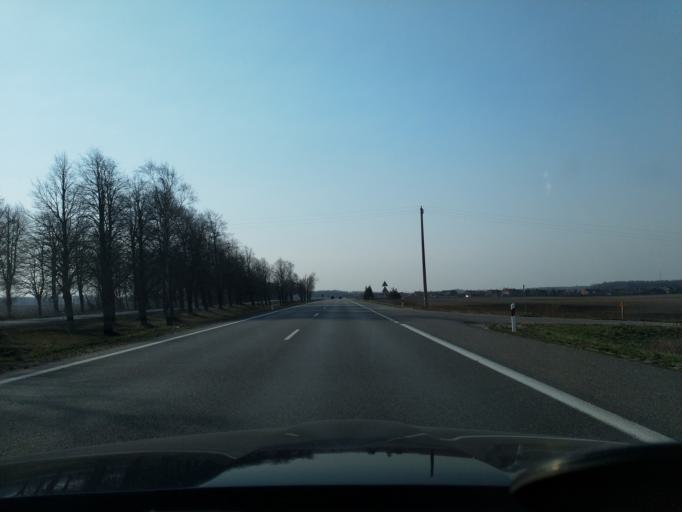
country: LT
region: Klaipedos apskritis
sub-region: Klaipeda
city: Klaipeda
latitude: 55.8144
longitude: 21.1269
